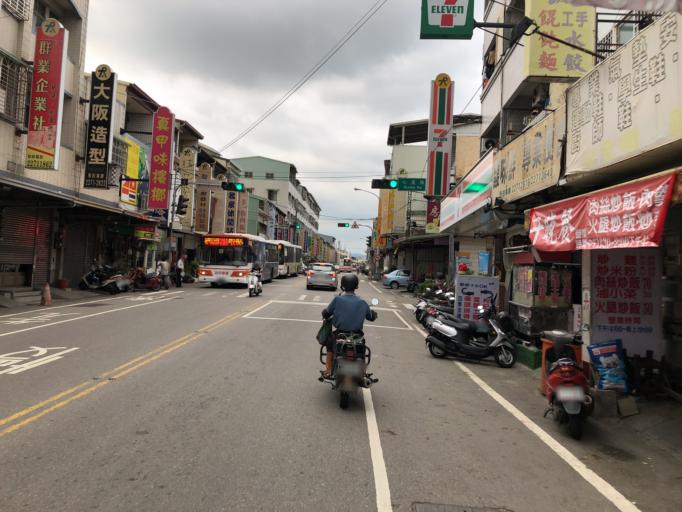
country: TW
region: Taiwan
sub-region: Taichung City
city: Taichung
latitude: 24.1038
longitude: 120.7290
